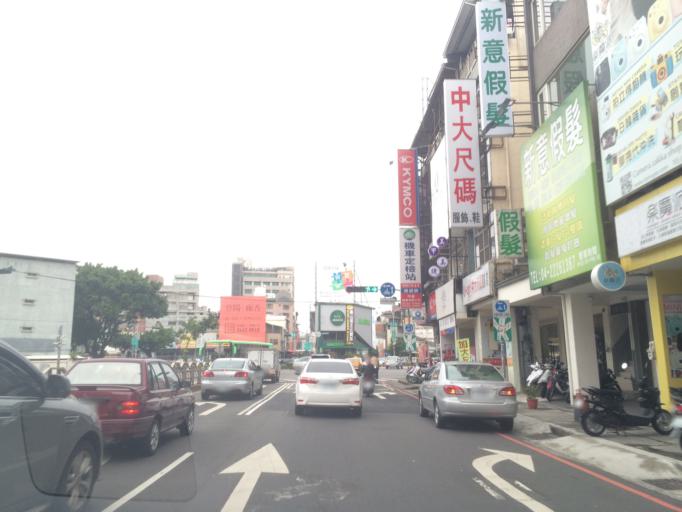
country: TW
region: Taiwan
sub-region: Taichung City
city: Taichung
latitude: 24.1542
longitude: 120.6860
